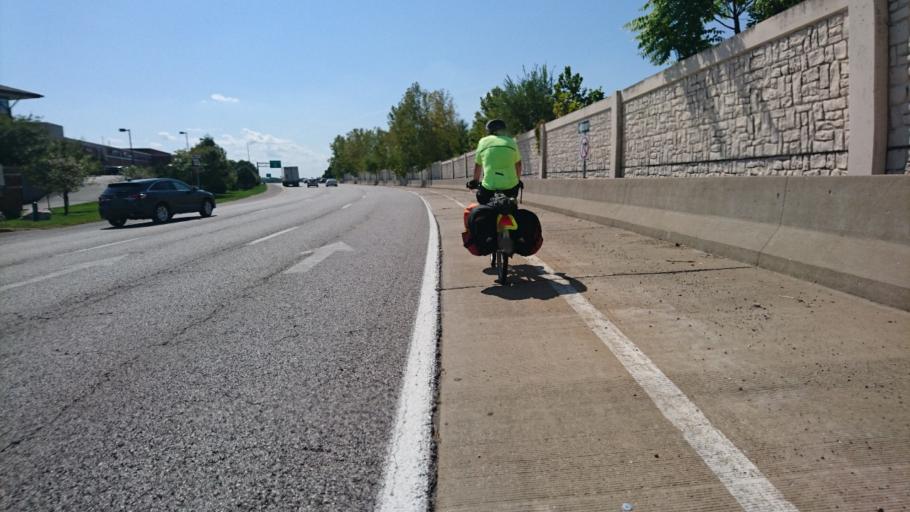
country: US
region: Missouri
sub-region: Saint Louis County
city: Town and Country
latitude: 38.6028
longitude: -90.4667
